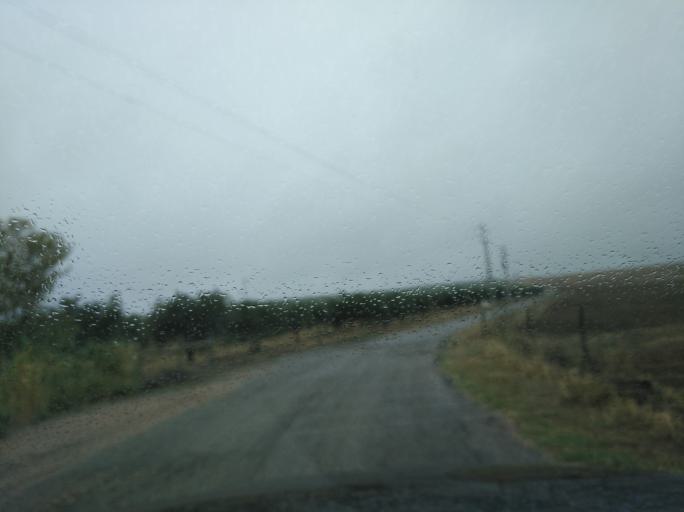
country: PT
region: Portalegre
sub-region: Campo Maior
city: Campo Maior
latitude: 38.9766
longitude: -7.0874
